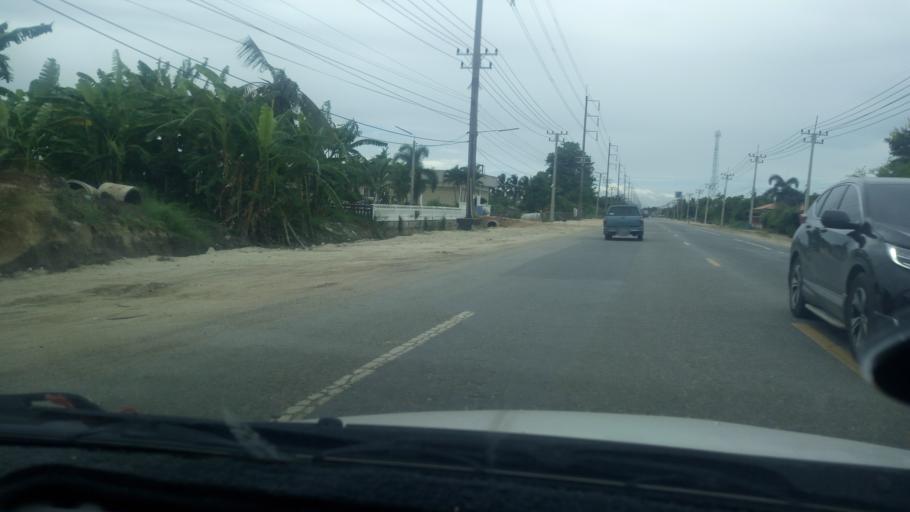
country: TH
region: Chon Buri
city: Phan Thong
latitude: 13.5180
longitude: 101.1548
